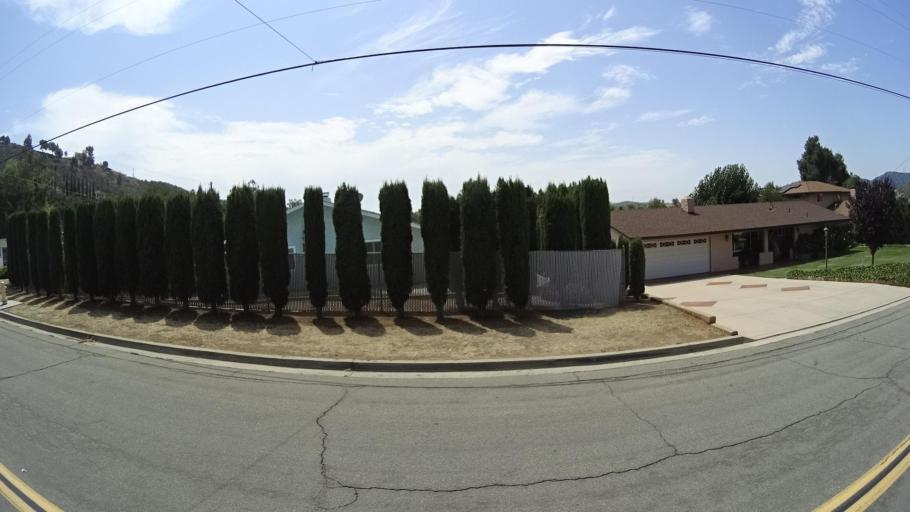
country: US
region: California
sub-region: San Diego County
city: Hidden Meadows
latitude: 33.1874
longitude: -117.0899
